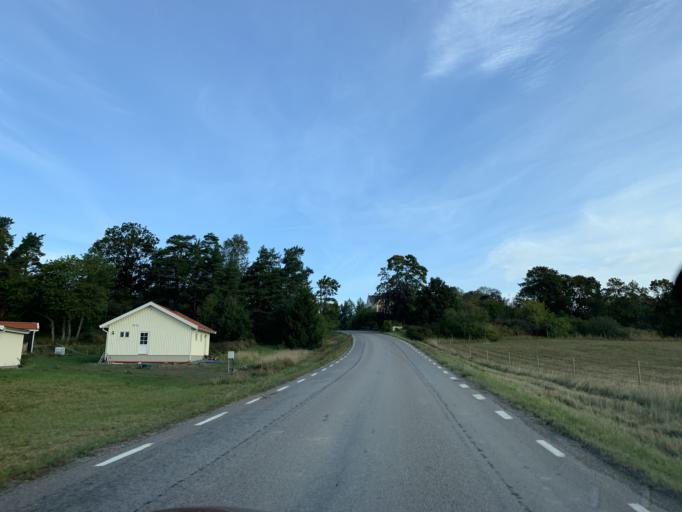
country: SE
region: Stockholm
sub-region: Haninge Kommun
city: Jordbro
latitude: 59.0643
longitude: 18.0666
